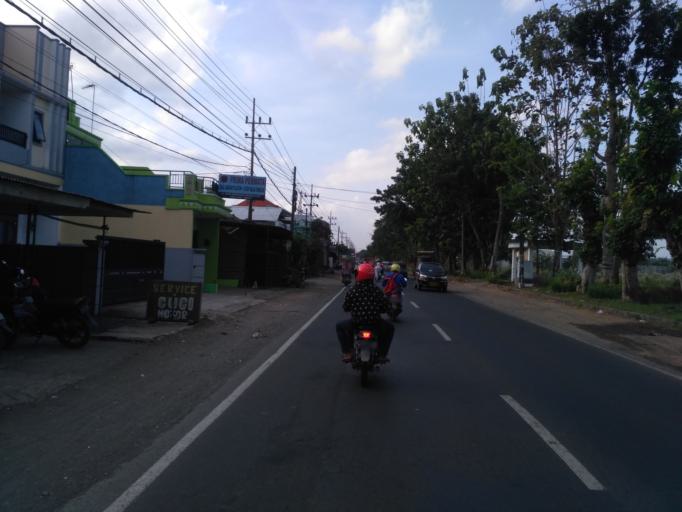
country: ID
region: East Java
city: Pakisaji
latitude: -8.0582
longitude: 112.6025
